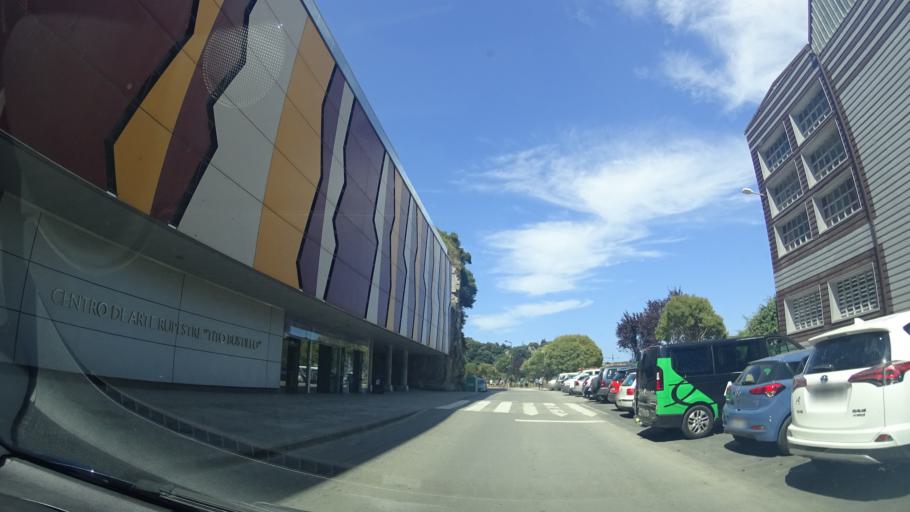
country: ES
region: Asturias
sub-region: Province of Asturias
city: Ribadesella
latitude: 43.4581
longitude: -5.0673
